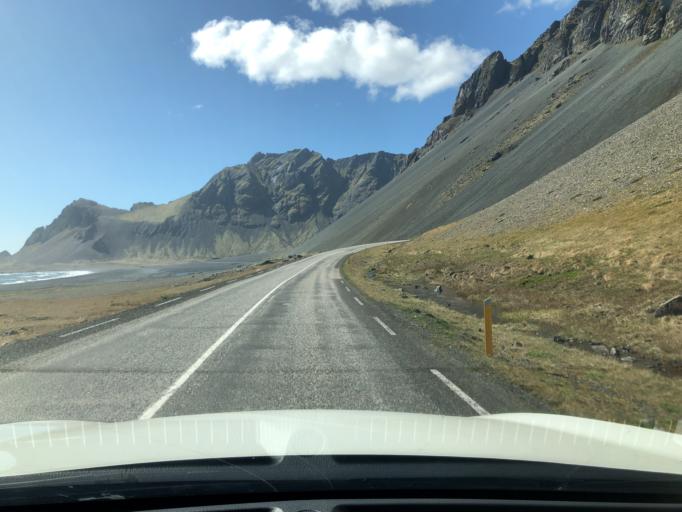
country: IS
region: East
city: Reydarfjoerdur
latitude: 64.4354
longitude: -14.5116
